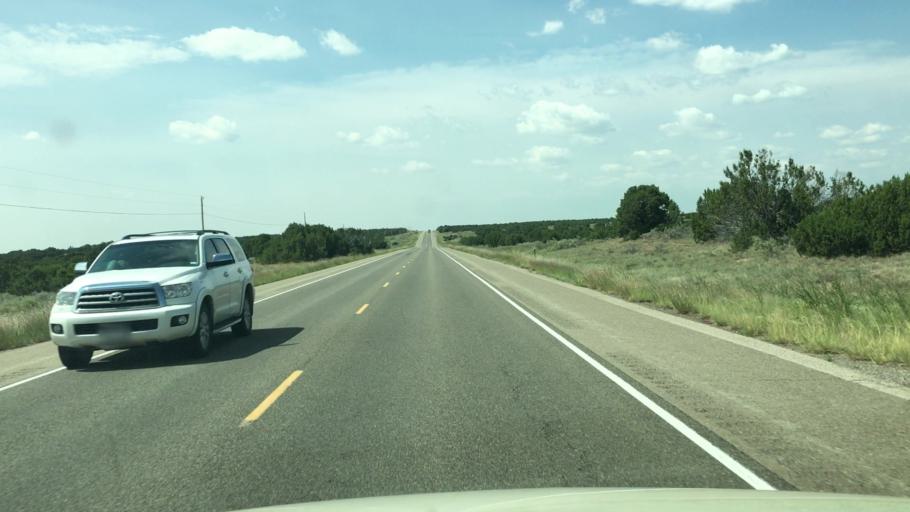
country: US
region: New Mexico
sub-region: Torrance County
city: Moriarty
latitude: 35.0488
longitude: -105.6868
